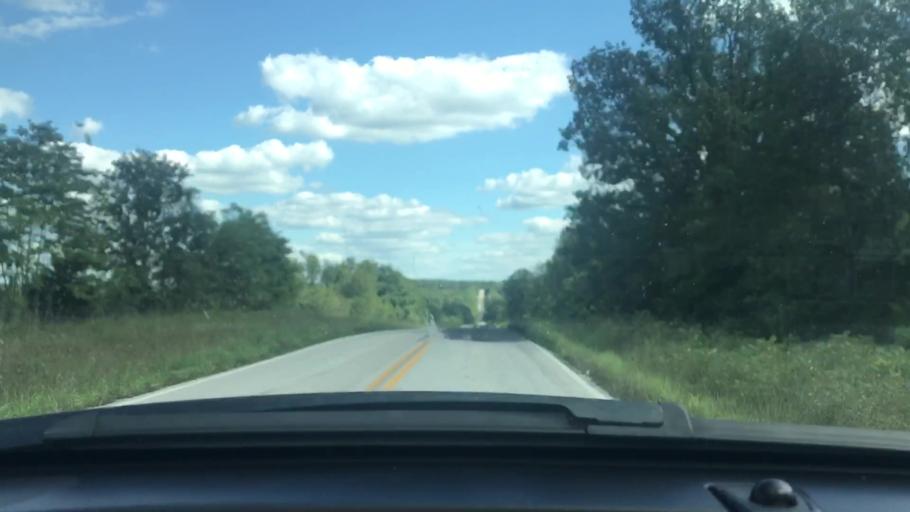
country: US
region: Missouri
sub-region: Wright County
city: Hartville
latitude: 37.3891
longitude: -92.4468
